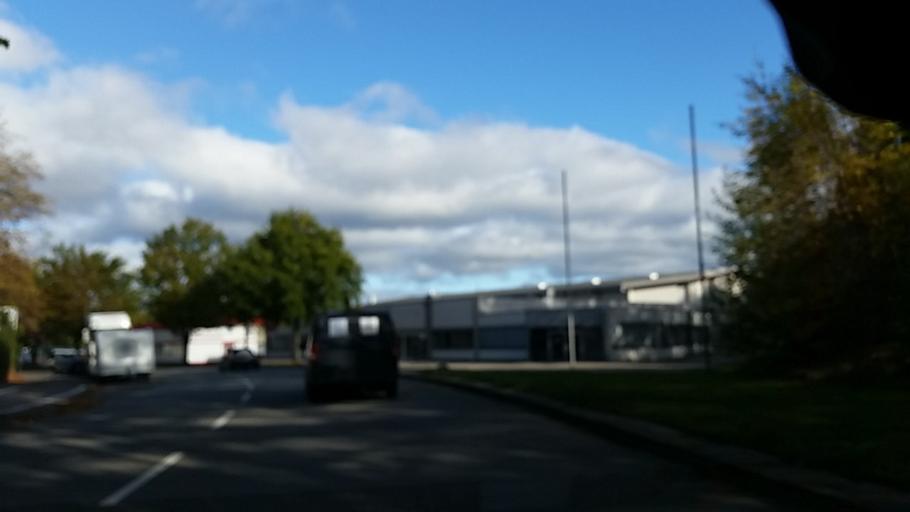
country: DE
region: Schleswig-Holstein
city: Oststeinbek
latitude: 53.5475
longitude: 10.1589
